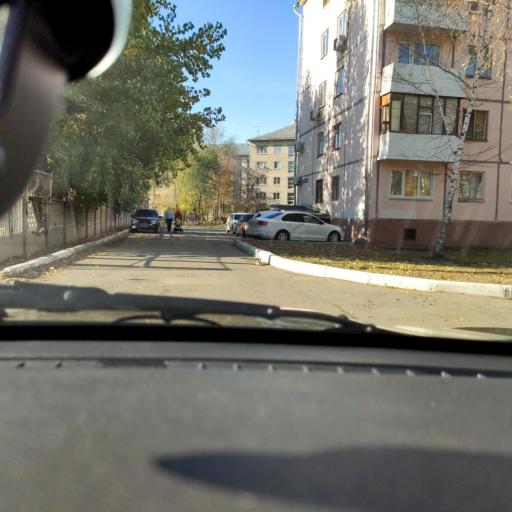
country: RU
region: Samara
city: Tol'yatti
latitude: 53.5128
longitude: 49.4251
